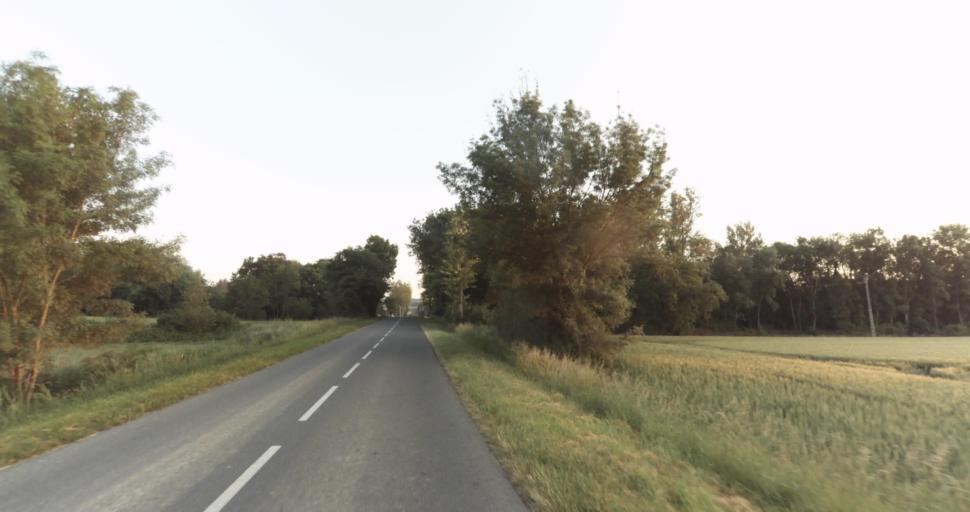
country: FR
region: Midi-Pyrenees
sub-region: Departement du Gers
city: Pujaudran
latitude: 43.6470
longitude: 1.1379
